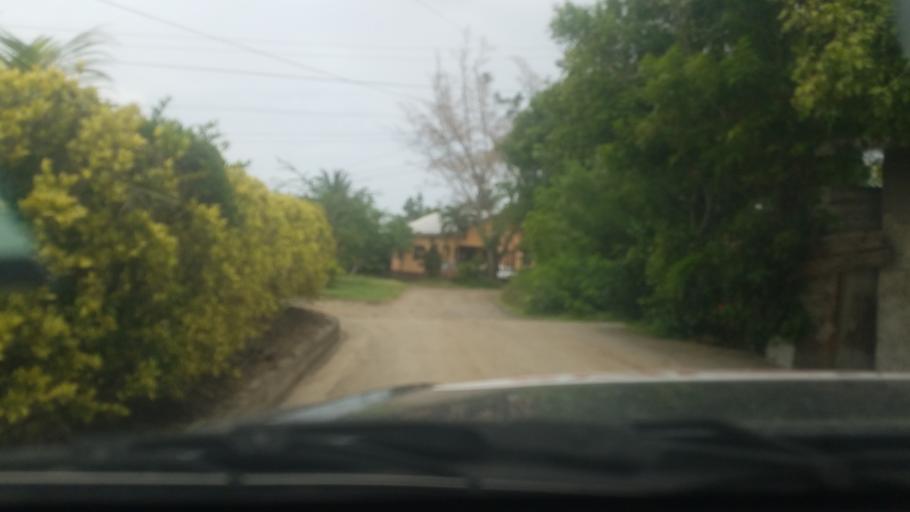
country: LC
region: Laborie Quarter
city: Laborie
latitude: 13.7494
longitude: -60.9791
